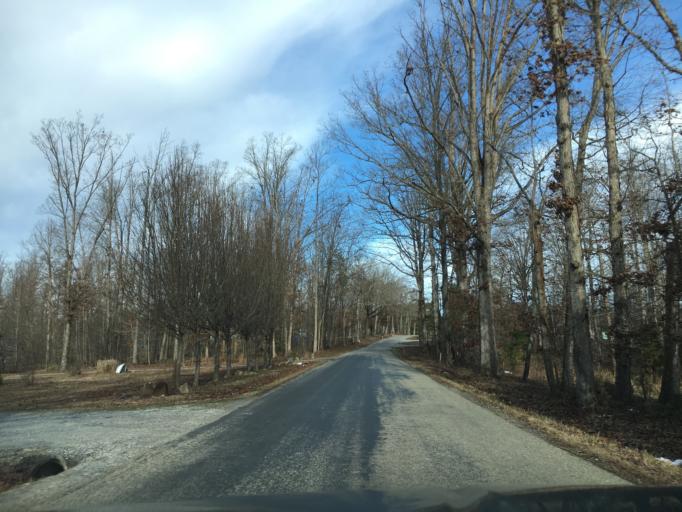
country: US
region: Virginia
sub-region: Nottoway County
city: Crewe
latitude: 37.2540
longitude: -78.2241
